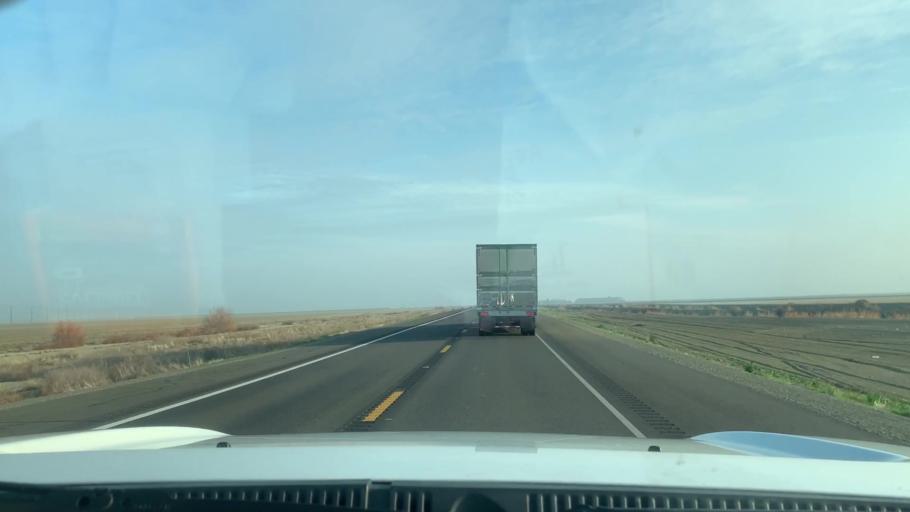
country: US
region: California
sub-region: Kings County
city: Kettleman City
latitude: 36.0396
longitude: -119.9569
